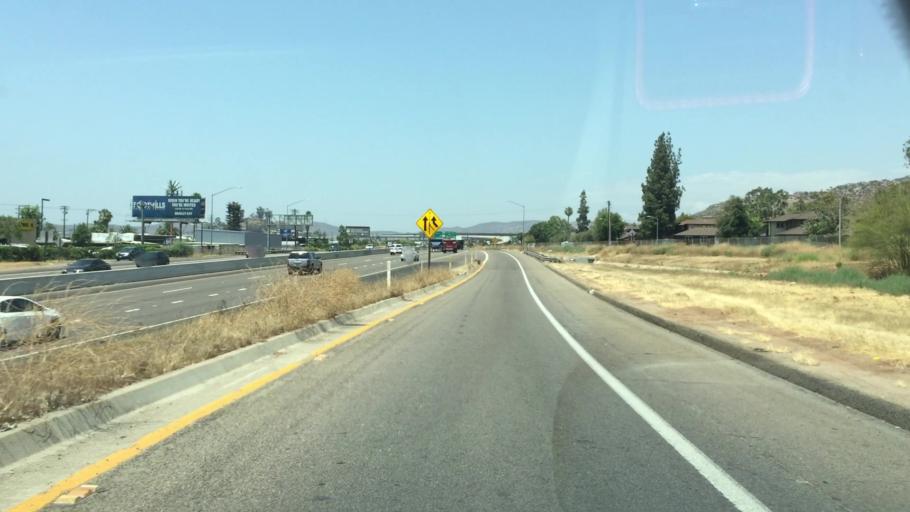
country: US
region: California
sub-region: San Diego County
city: Santee
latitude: 32.8201
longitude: -116.9603
